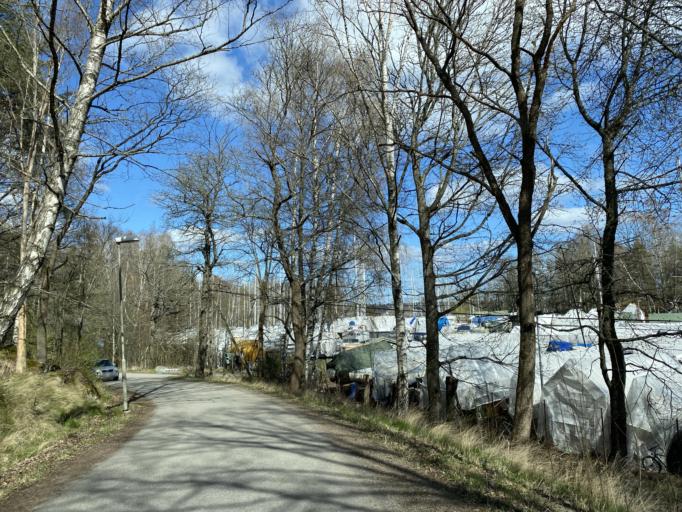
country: SE
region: Stockholm
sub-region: Nacka Kommun
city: Nacka
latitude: 59.3290
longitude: 18.1494
